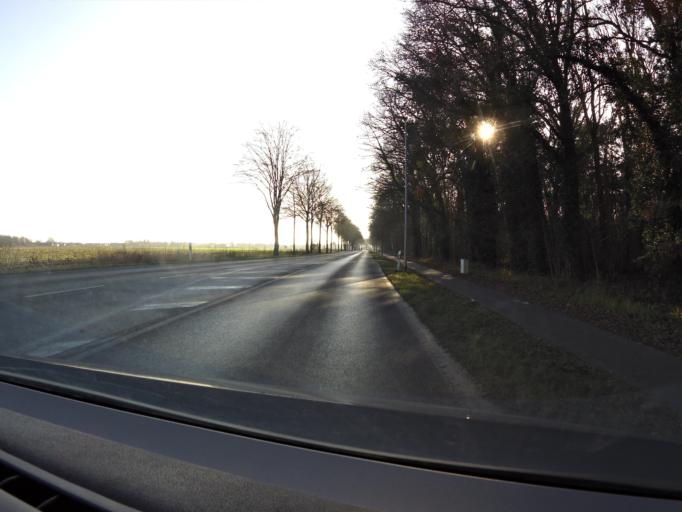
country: DE
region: North Rhine-Westphalia
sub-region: Regierungsbezirk Dusseldorf
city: Bruggen
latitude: 51.2672
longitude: 6.1878
